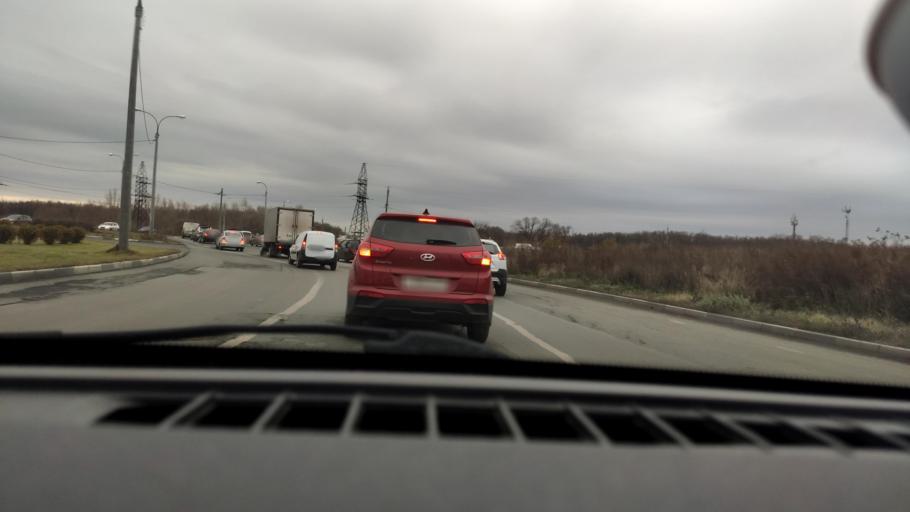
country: RU
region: Samara
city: Samara
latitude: 53.1347
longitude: 50.1733
